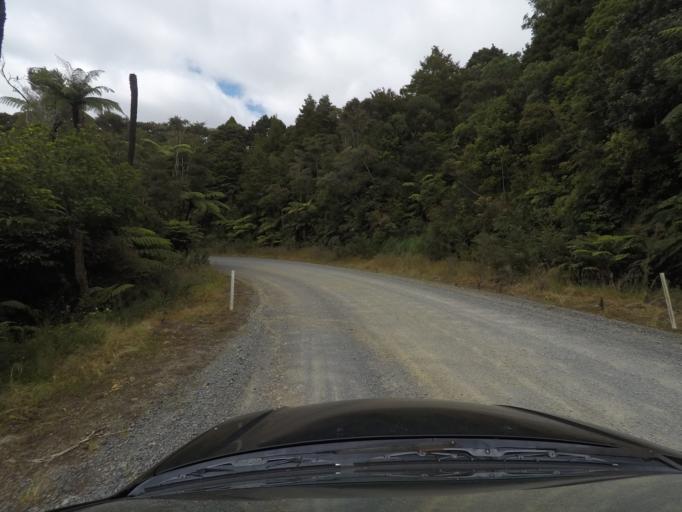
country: NZ
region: Northland
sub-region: Whangarei
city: Ruakaka
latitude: -35.9264
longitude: 174.3381
